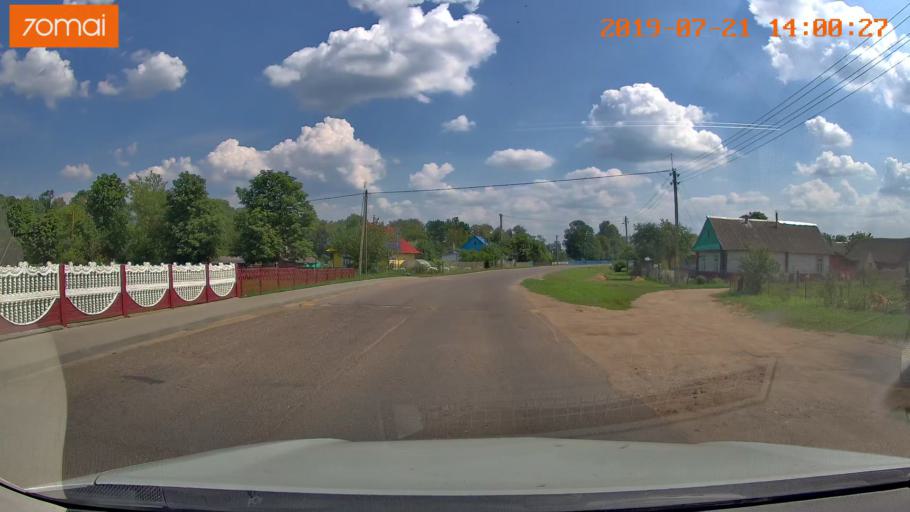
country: BY
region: Grodnenskaya
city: Lyubcha
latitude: 53.7502
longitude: 26.0649
